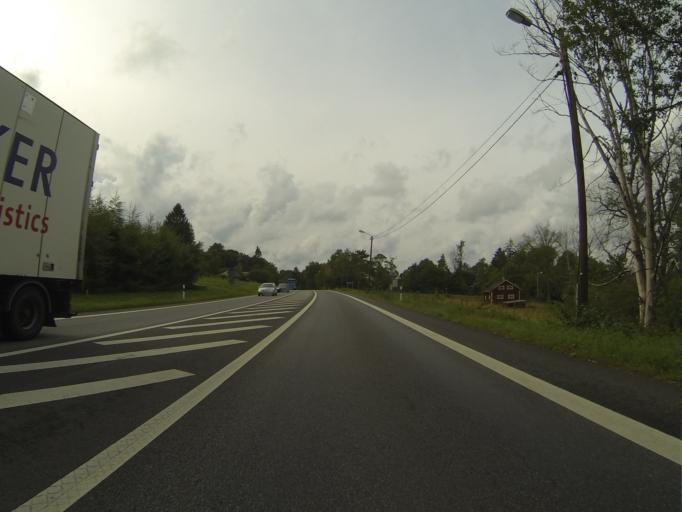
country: SE
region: Skane
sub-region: Kristianstads Kommun
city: Onnestad
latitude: 55.9422
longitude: 13.9024
